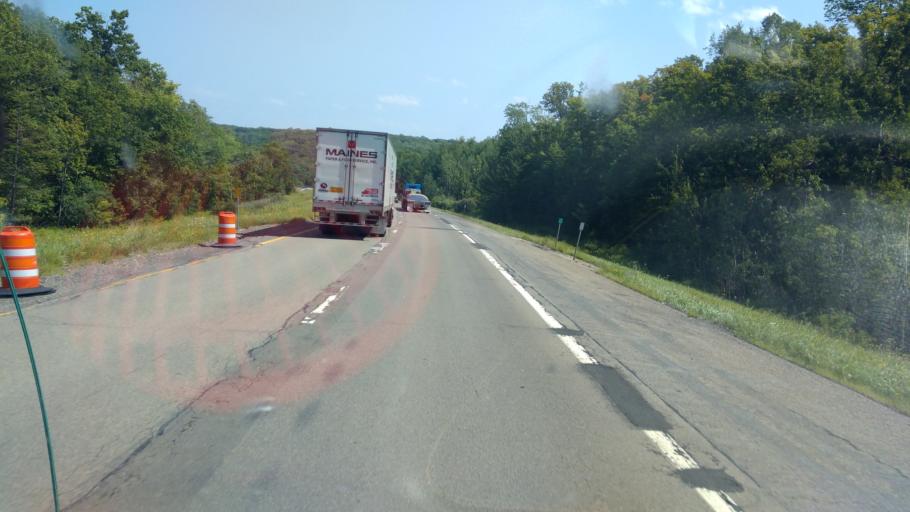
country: US
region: New York
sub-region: Allegany County
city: Alfred
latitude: 42.3120
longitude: -77.8503
